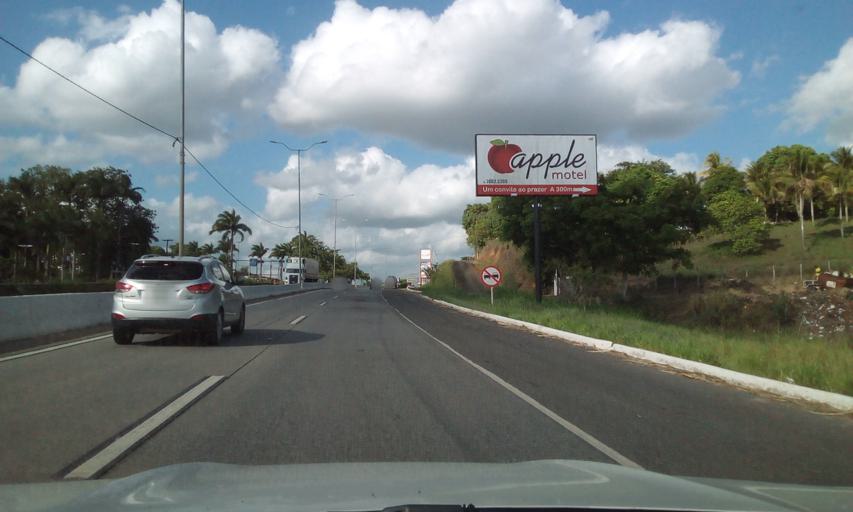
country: BR
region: Pernambuco
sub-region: Palmares
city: Palmares
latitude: -8.6716
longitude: -35.5757
